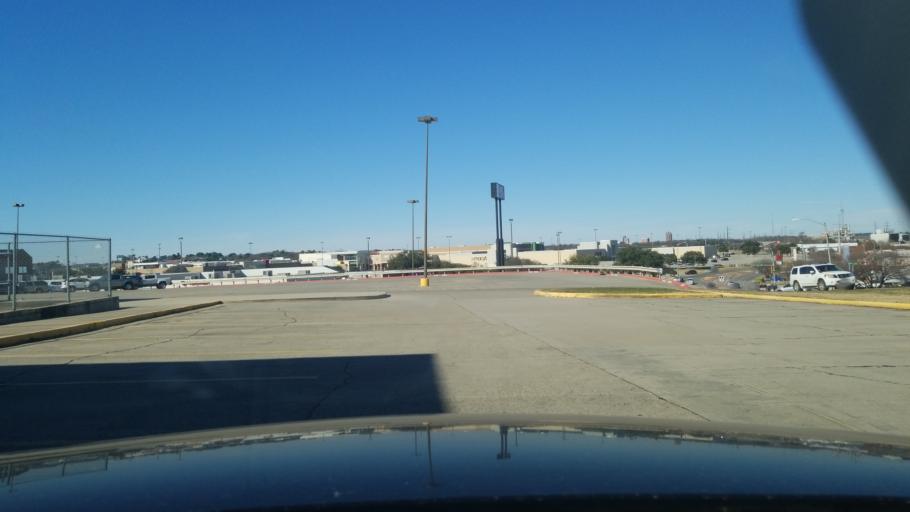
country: US
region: Texas
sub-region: Denton County
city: Denton
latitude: 33.1876
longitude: -97.1034
